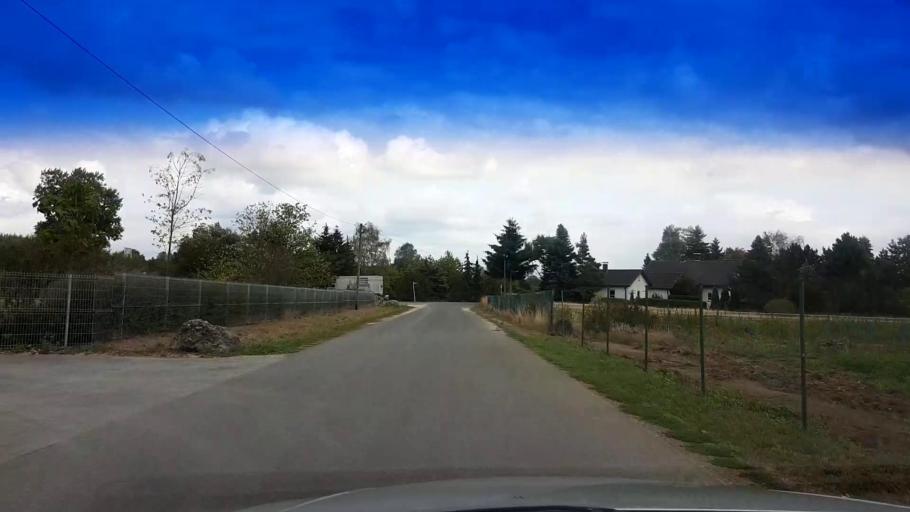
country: DE
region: Bavaria
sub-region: Upper Franconia
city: Bamberg
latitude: 49.8780
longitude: 10.9218
